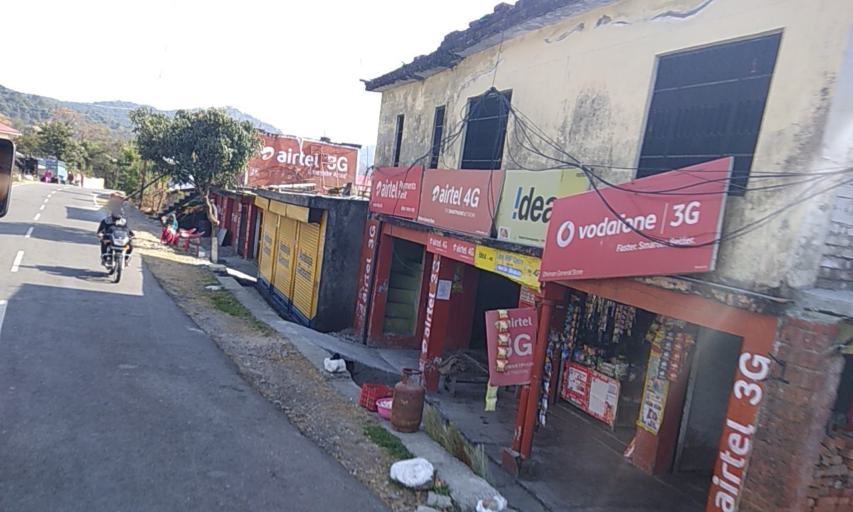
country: IN
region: Himachal Pradesh
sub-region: Kangra
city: Dharmsala
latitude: 32.1588
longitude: 76.4109
